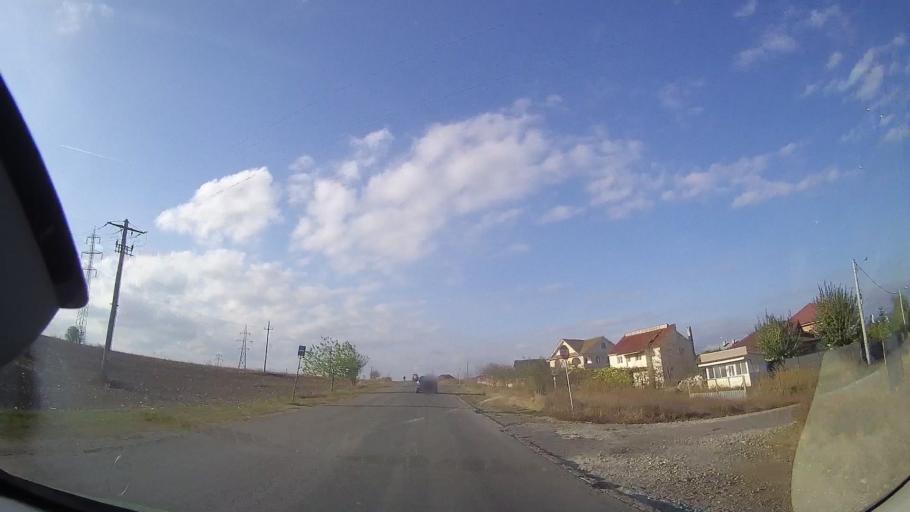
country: RO
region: Constanta
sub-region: Comuna Limanu
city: Limanu
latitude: 43.7924
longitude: 28.5459
